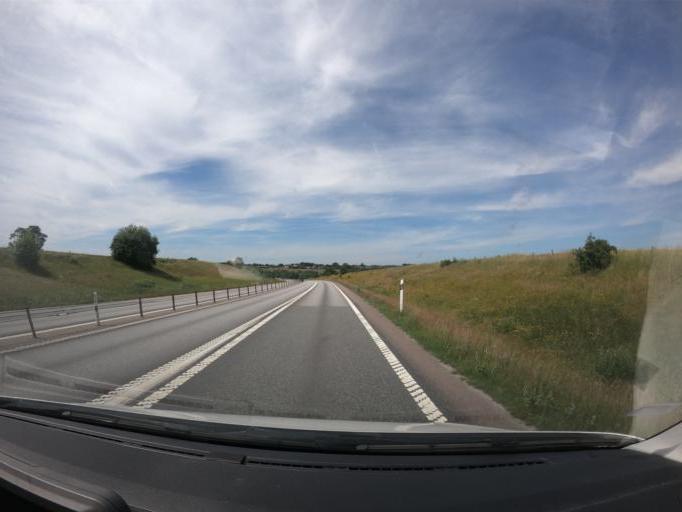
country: SE
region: Skane
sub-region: Klippans Kommun
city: Klippan
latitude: 56.1258
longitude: 13.0995
